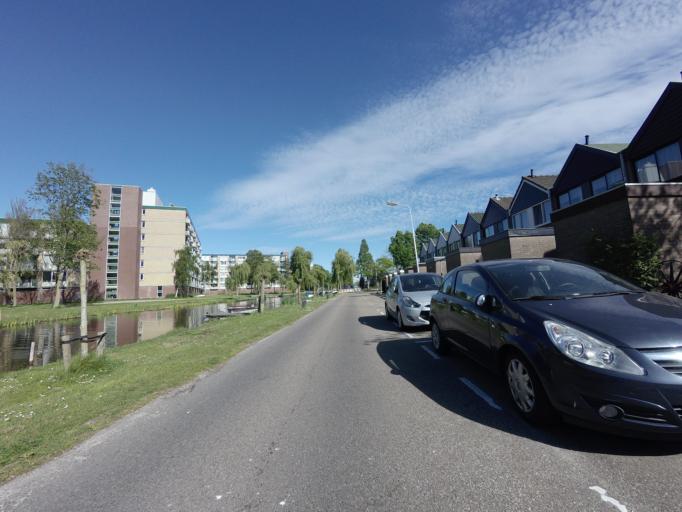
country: NL
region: North Holland
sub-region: Gemeente Uitgeest
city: Uitgeest
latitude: 52.5050
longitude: 4.7498
